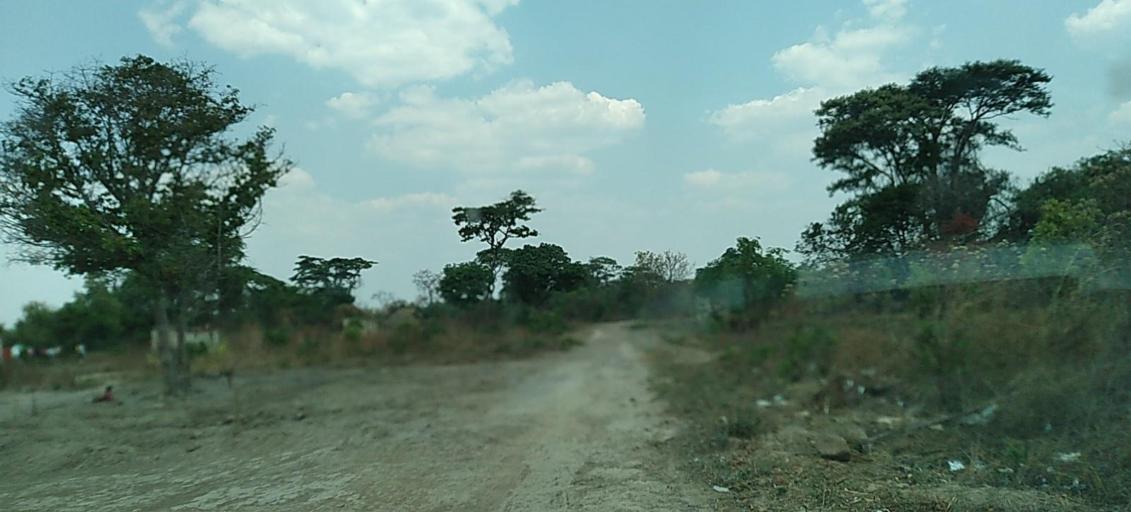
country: CD
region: Katanga
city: Kipushi
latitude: -11.9929
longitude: 27.4179
